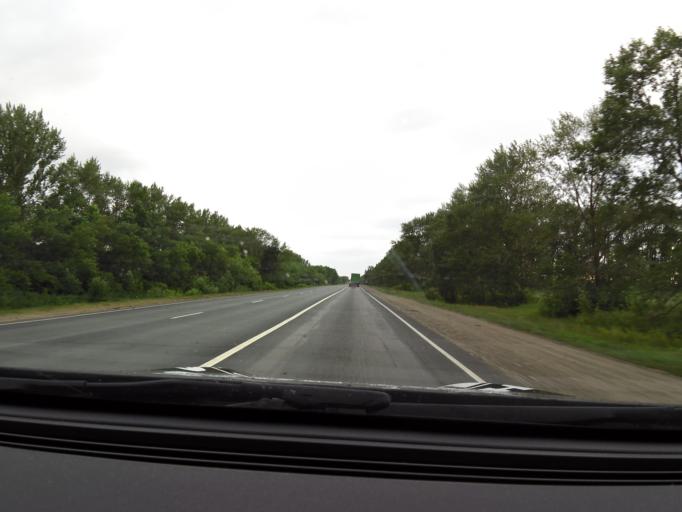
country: RU
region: Chuvashia
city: Yantikovo
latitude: 55.7908
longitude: 47.7686
